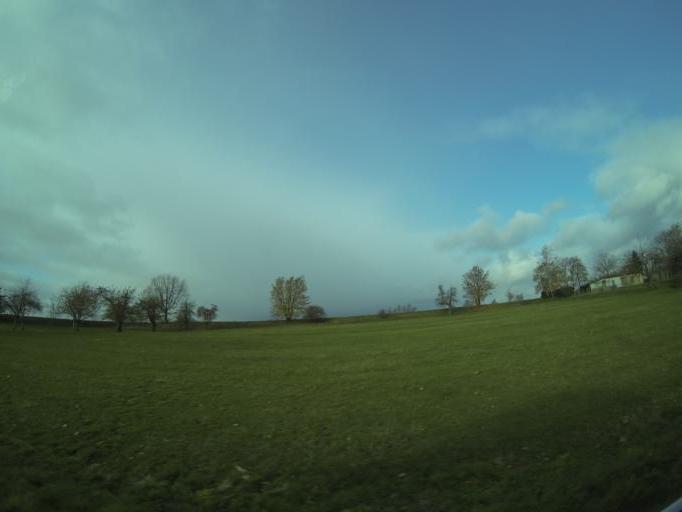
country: DE
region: Thuringia
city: Gossnitz
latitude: 50.8914
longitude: 12.3950
